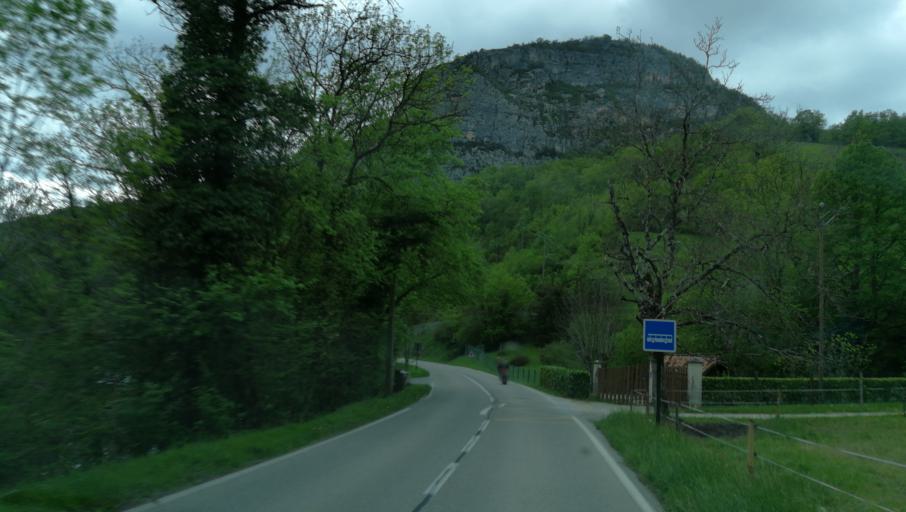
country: FR
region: Rhone-Alpes
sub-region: Departement de l'Isere
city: Pont-en-Royans
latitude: 45.0665
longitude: 5.3611
